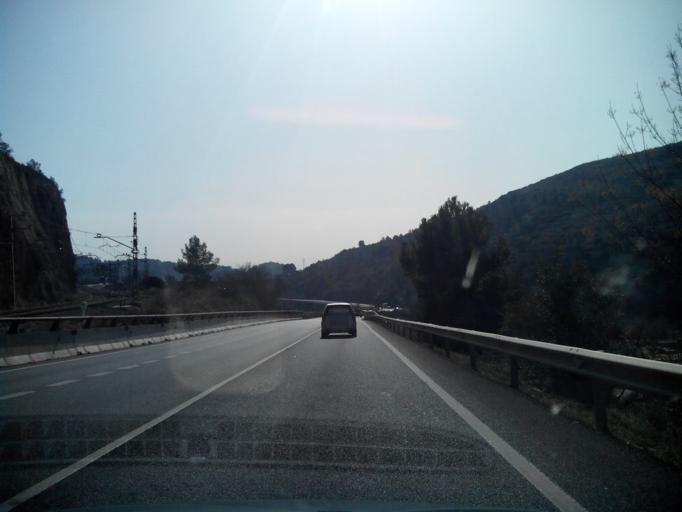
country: ES
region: Catalonia
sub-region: Provincia de Tarragona
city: Alcover
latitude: 41.3087
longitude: 1.1911
